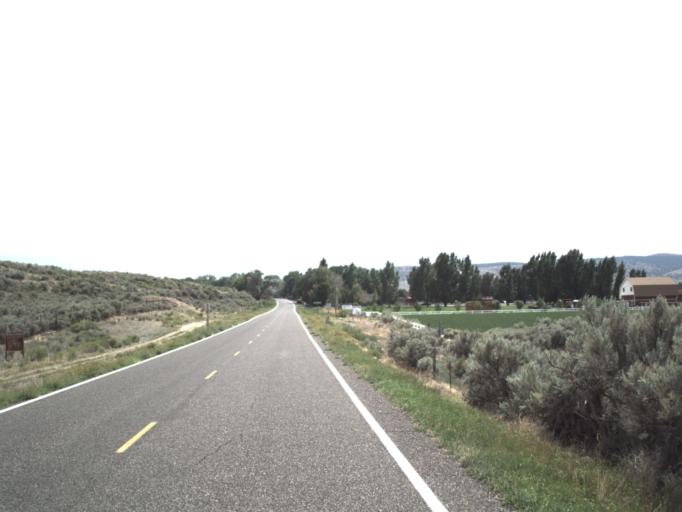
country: US
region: Utah
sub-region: Piute County
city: Junction
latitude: 38.1296
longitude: -112.0003
